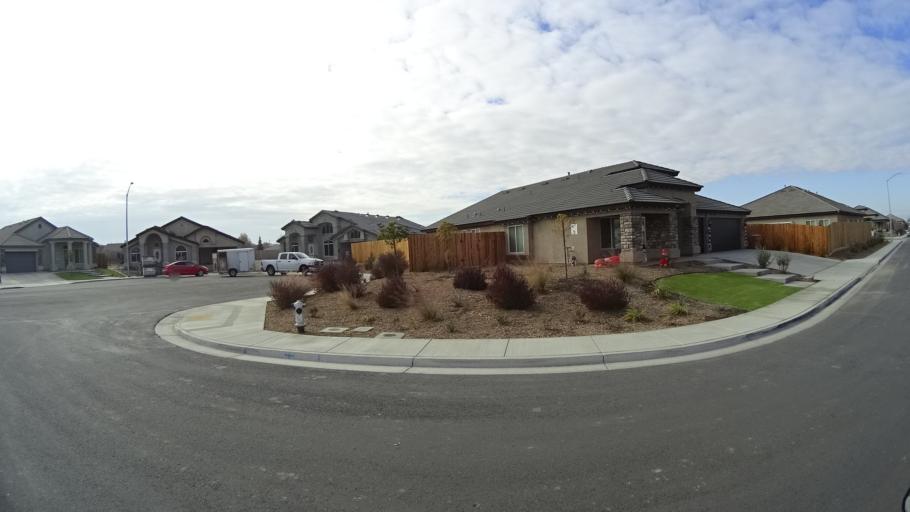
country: US
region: California
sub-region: Kern County
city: Rosedale
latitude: 35.3007
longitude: -119.1342
